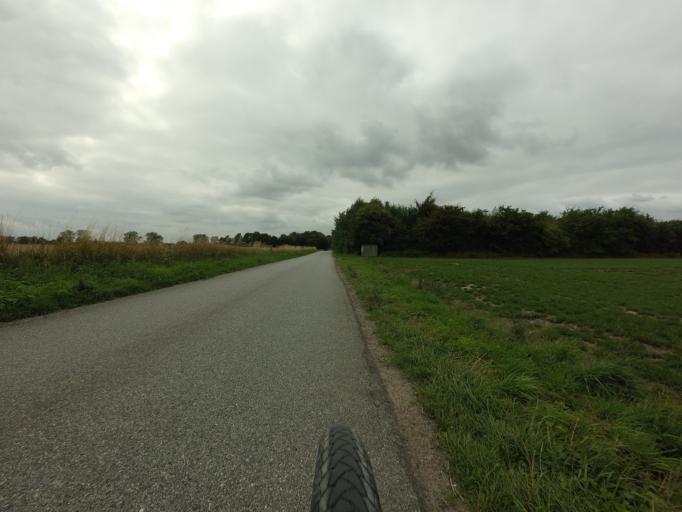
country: DK
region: Zealand
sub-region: Stevns Kommune
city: Store Heddinge
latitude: 55.3388
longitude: 12.4286
